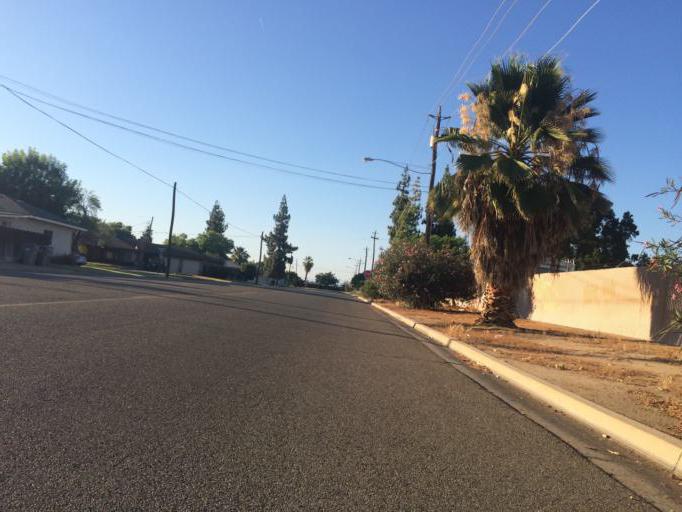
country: US
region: California
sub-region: Fresno County
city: Tarpey Village
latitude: 36.7767
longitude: -119.7317
